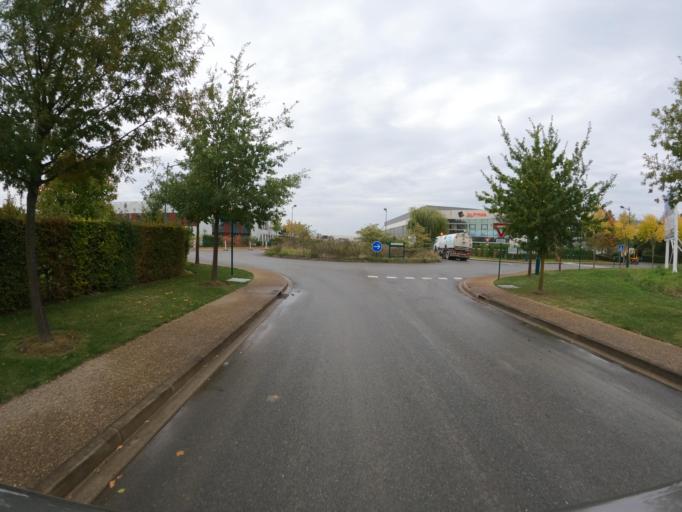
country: FR
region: Ile-de-France
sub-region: Departement de Seine-et-Marne
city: Serris
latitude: 48.8421
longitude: 2.7970
